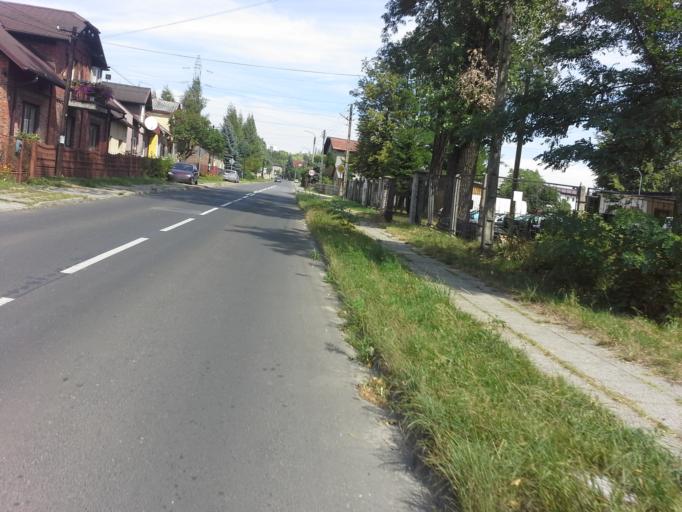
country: PL
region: Lesser Poland Voivodeship
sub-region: Powiat chrzanowski
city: Trzebinia
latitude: 50.1533
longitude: 19.4692
